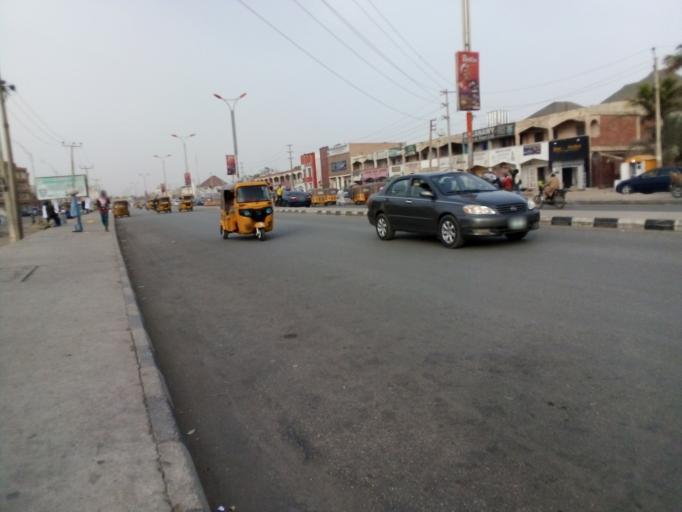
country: NG
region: Kano
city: Kano
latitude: 11.9755
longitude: 8.5355
